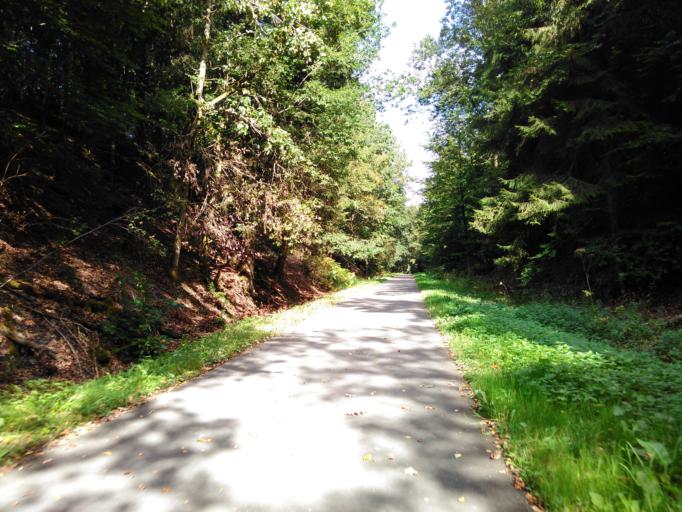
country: BE
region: Wallonia
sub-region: Province du Luxembourg
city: Gouvy
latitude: 50.1250
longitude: 5.9066
